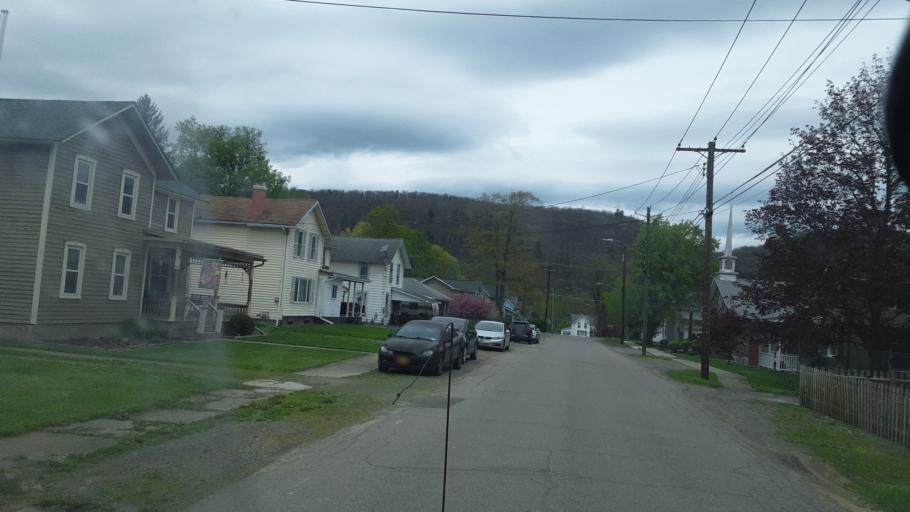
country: US
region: New York
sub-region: Steuben County
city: Addison
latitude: 42.1032
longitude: -77.2429
